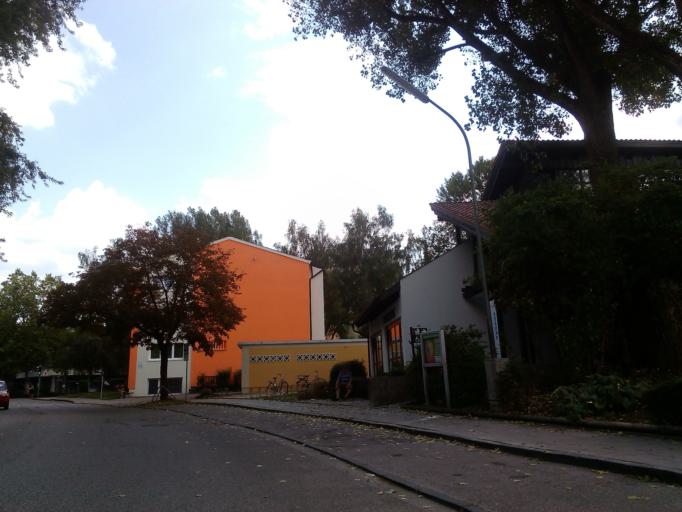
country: DE
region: Bavaria
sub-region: Upper Bavaria
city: Puchheim
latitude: 48.1710
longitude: 11.3504
